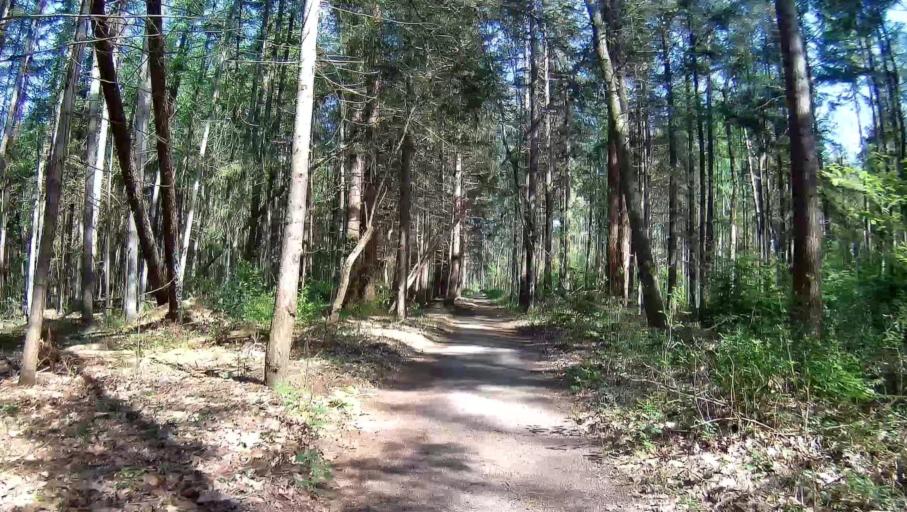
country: NL
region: Drenthe
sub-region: Gemeente Borger-Odoorn
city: Borger
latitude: 52.9581
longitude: 6.7834
